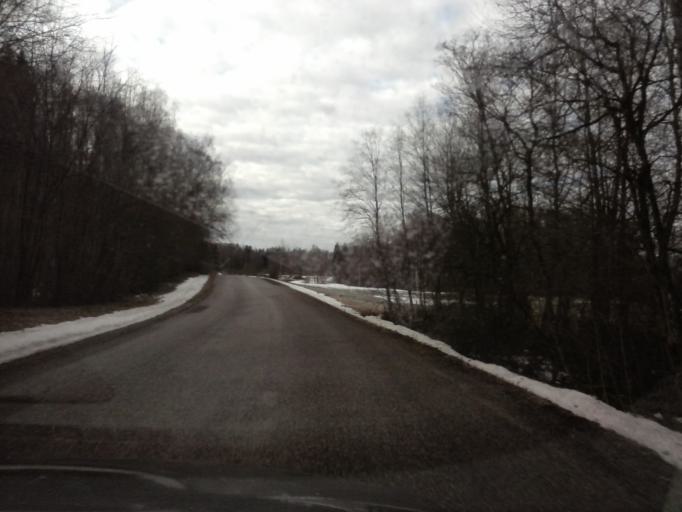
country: EE
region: Tartu
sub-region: Elva linn
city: Elva
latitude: 58.0091
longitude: 26.2945
